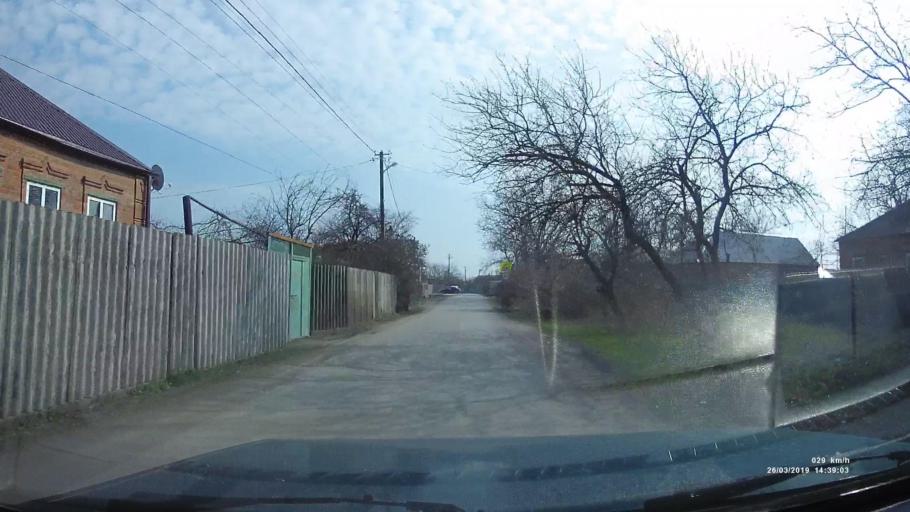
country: RU
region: Rostov
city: Novobessergenovka
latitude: 47.1799
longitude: 38.8625
